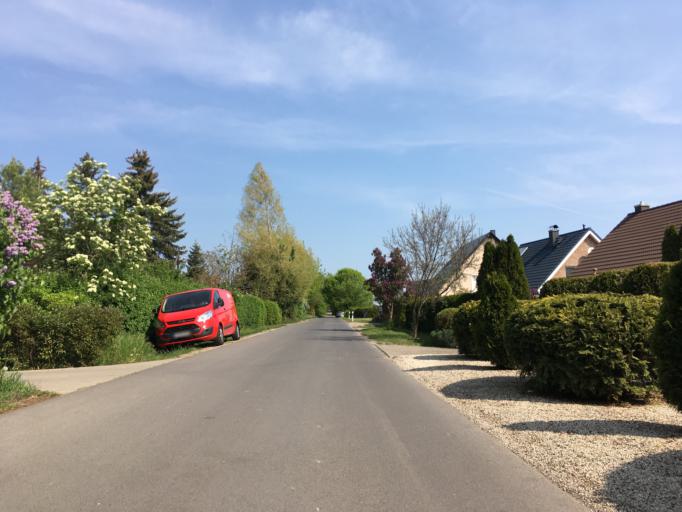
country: DE
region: Brandenburg
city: Altlandsberg
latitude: 52.5815
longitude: 13.7255
